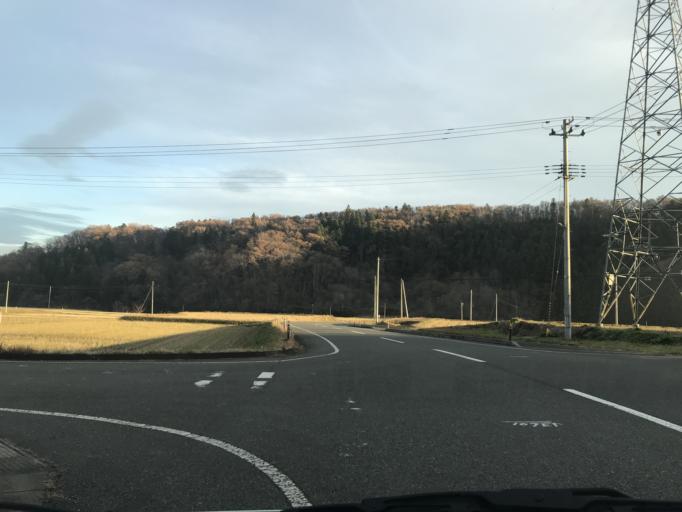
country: JP
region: Iwate
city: Ichinoseki
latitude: 38.9726
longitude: 141.0749
